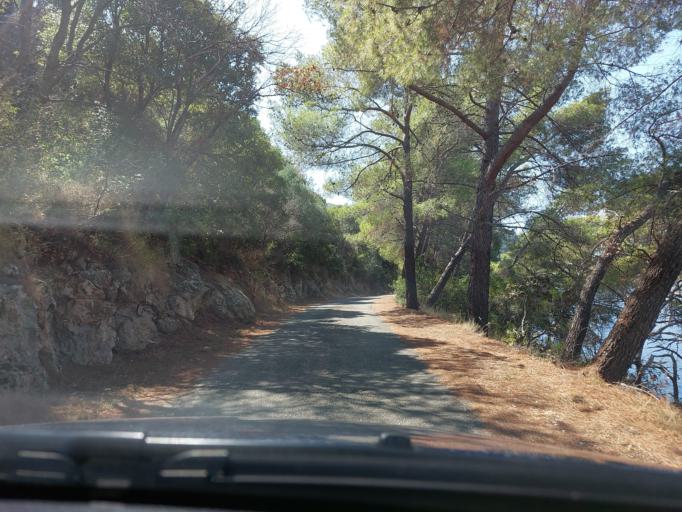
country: HR
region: Dubrovacko-Neretvanska
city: Smokvica
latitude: 42.7707
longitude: 16.8373
